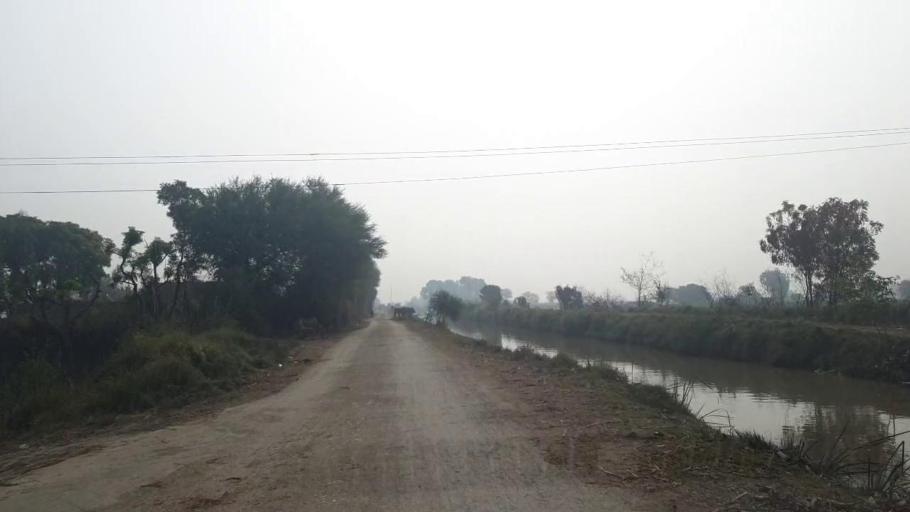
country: PK
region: Sindh
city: Tando Adam
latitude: 25.7567
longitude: 68.6150
